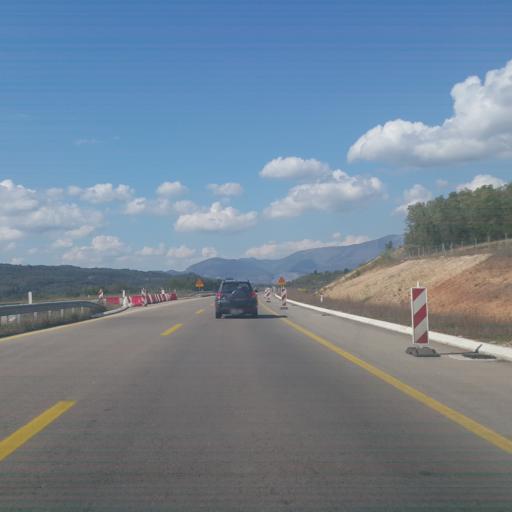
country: RS
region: Central Serbia
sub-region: Pirotski Okrug
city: Bela Palanka
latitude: 43.2405
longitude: 22.2860
